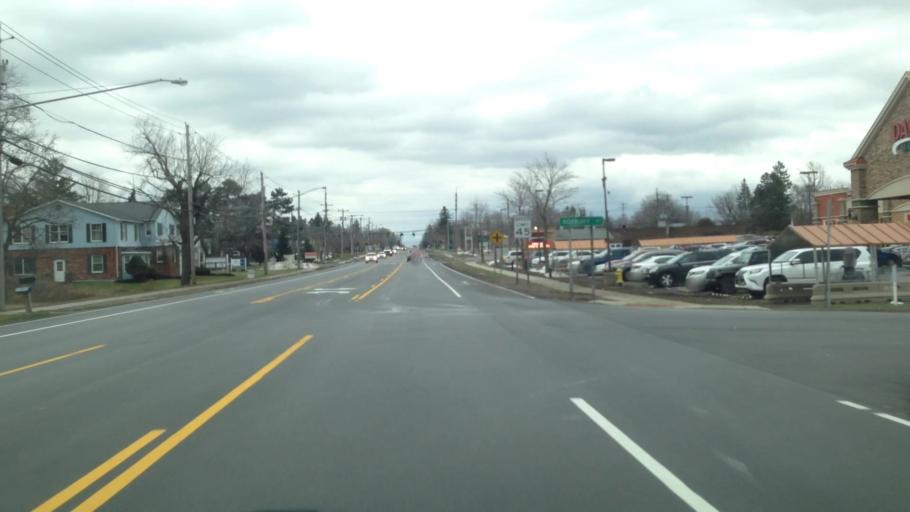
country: US
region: New York
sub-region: Erie County
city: Harris Hill
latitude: 42.9663
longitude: -78.6630
